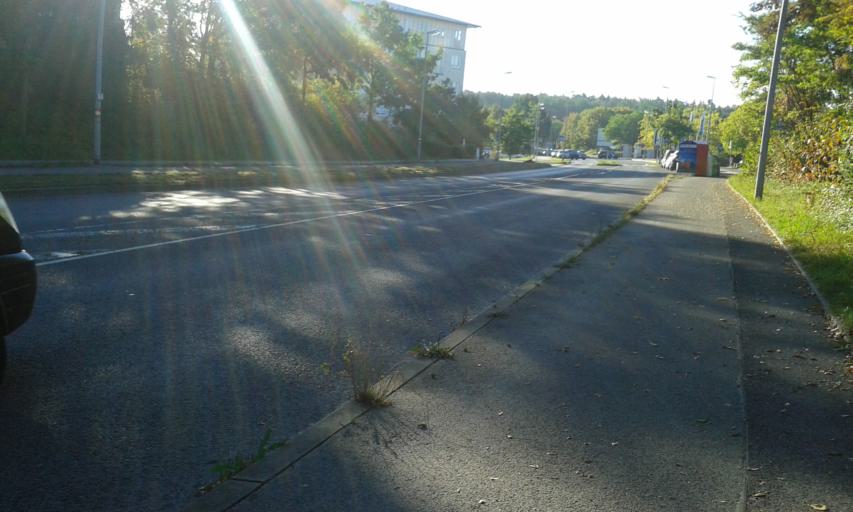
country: DE
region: Bavaria
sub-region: Upper Franconia
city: Bamberg
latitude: 49.8706
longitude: 10.8905
